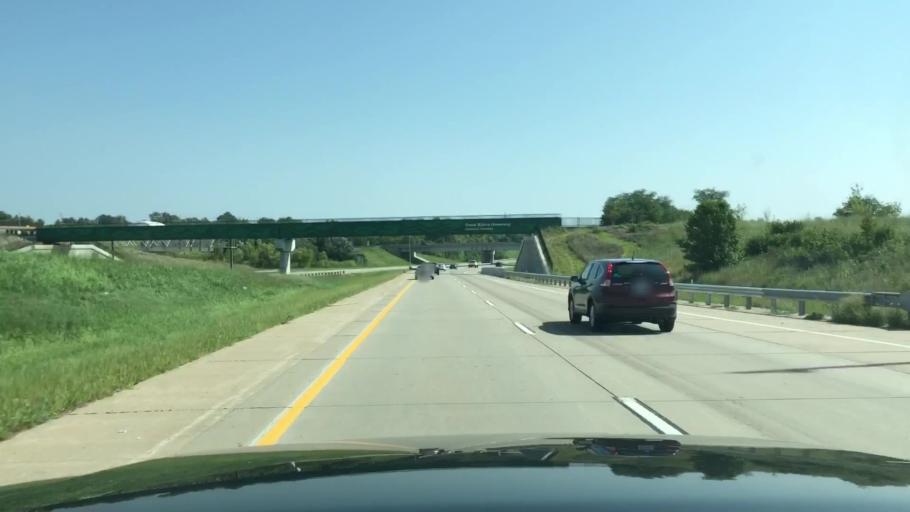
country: US
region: Missouri
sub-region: Saint Charles County
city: Saint Charles
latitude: 38.7549
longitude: -90.5459
